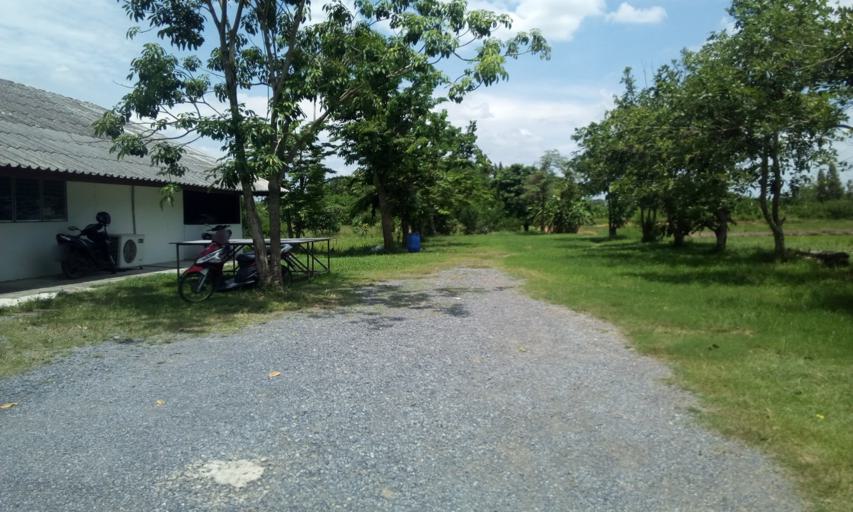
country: TH
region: Pathum Thani
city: Ban Lam Luk Ka
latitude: 13.9895
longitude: 100.8427
